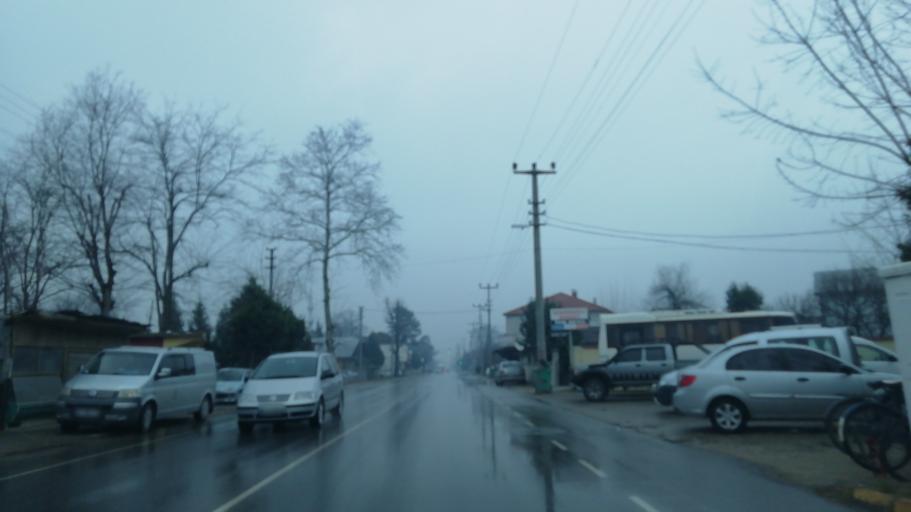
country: TR
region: Sakarya
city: Akyazi
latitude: 40.6544
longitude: 30.6166
